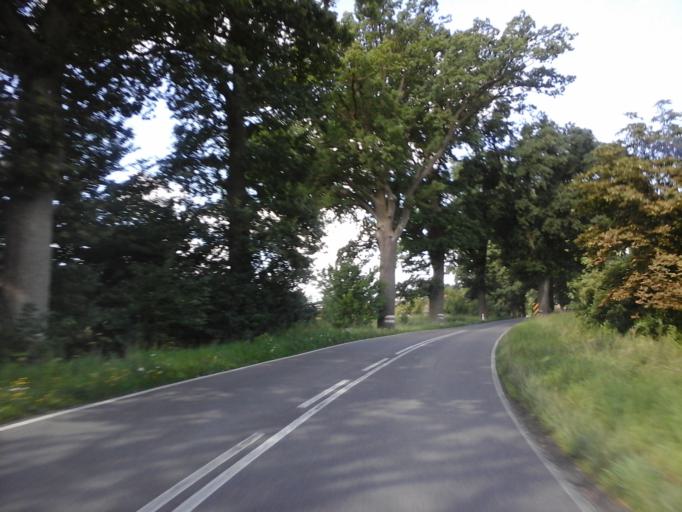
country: PL
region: West Pomeranian Voivodeship
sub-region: Powiat stargardzki
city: Dolice
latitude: 53.1980
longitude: 15.2617
